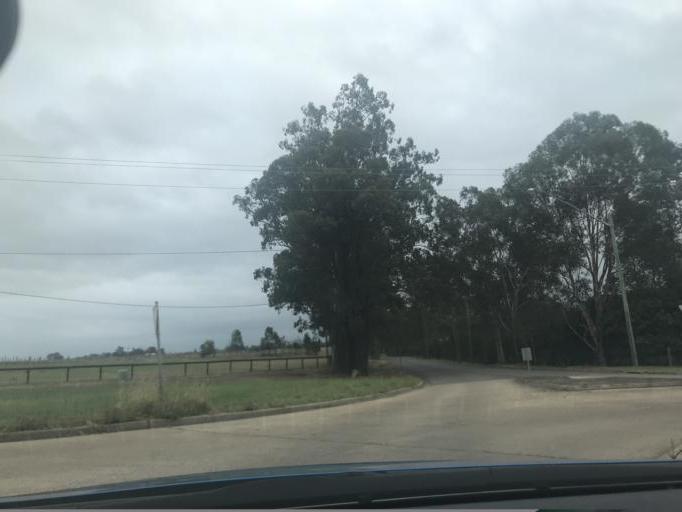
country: AU
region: New South Wales
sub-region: Cessnock
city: Cessnock
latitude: -32.8261
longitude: 151.3226
